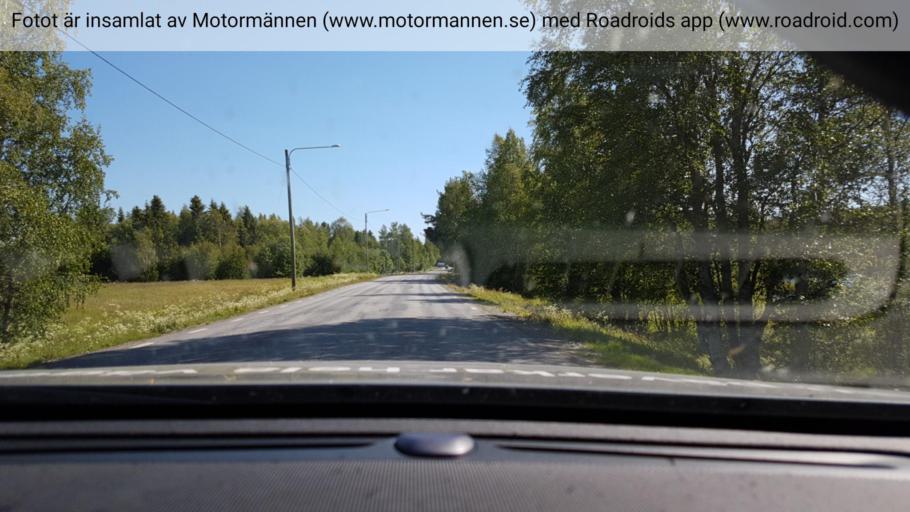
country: SE
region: Vaesterbotten
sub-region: Vilhelmina Kommun
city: Sjoberg
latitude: 64.6781
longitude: 16.2907
